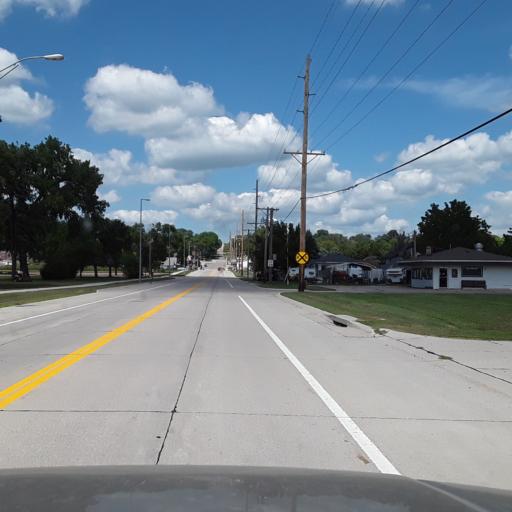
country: US
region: Nebraska
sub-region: Nance County
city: Genoa
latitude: 41.4448
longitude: -97.7346
